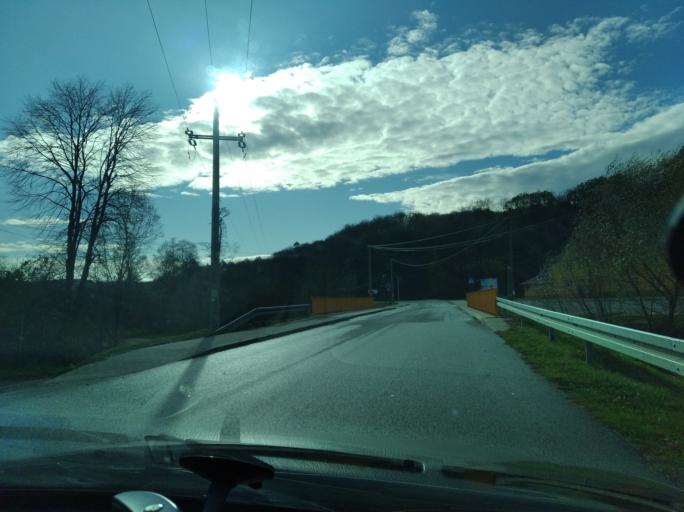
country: PL
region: Subcarpathian Voivodeship
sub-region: Powiat debicki
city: Brzeznica
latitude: 50.0493
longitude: 21.4865
